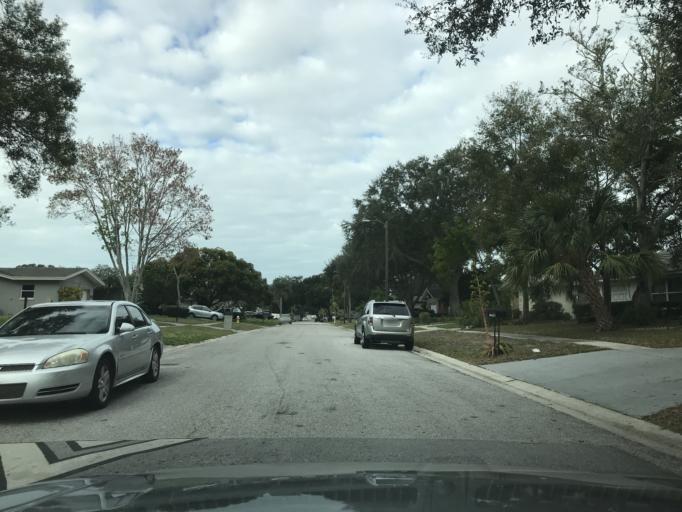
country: US
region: Florida
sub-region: Pinellas County
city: Largo
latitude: 27.9356
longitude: -82.7756
